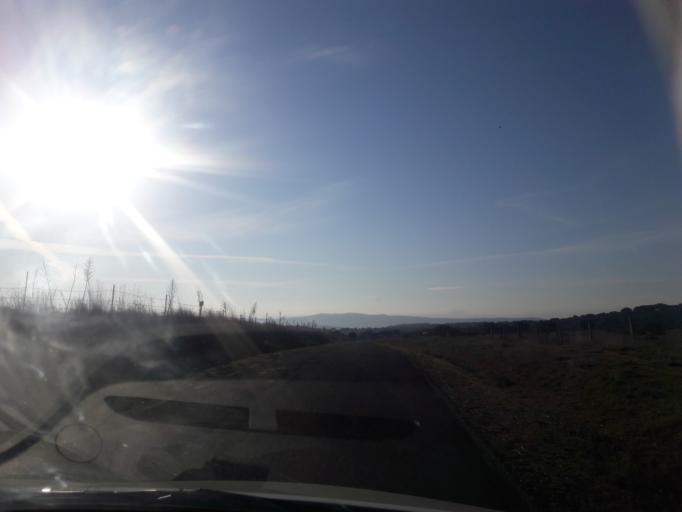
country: ES
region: Castille and Leon
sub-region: Provincia de Salamanca
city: Montejo
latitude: 40.6259
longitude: -5.6144
